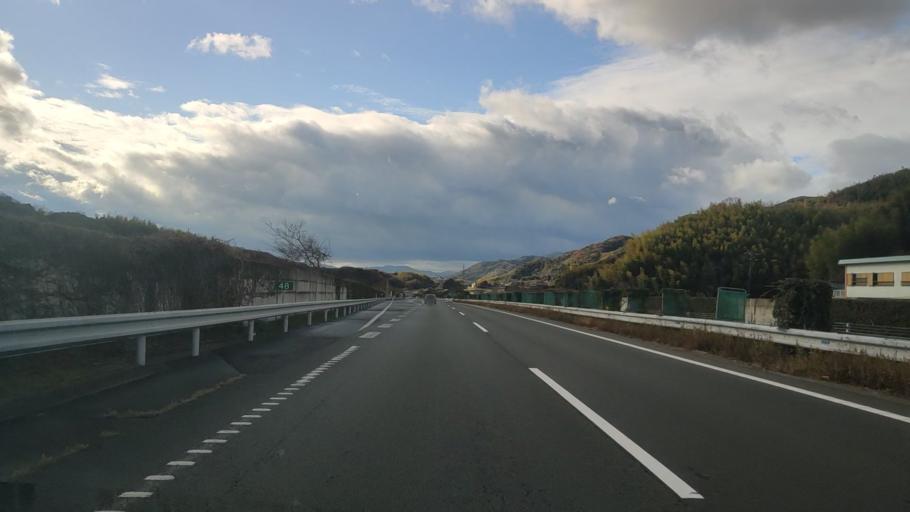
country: JP
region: Hyogo
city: Sumoto
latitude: 34.4115
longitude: 134.8656
